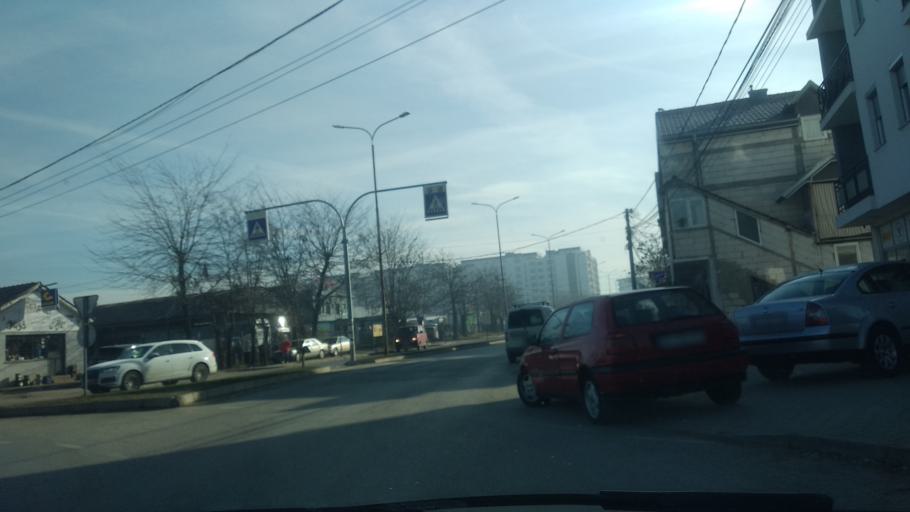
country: XK
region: Mitrovica
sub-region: Vushtrri
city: Vushtrri
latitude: 42.8201
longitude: 20.9764
